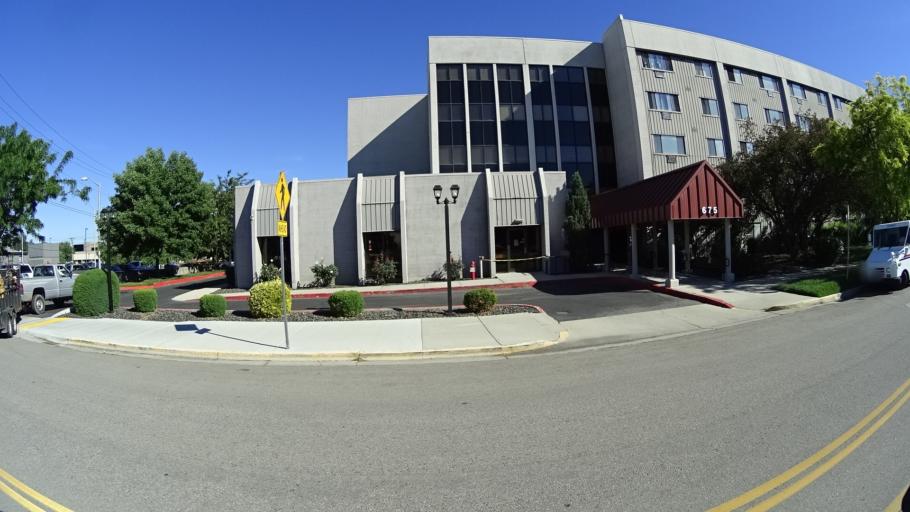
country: US
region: Idaho
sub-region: Ada County
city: Boise
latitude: 43.6146
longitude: -116.2163
